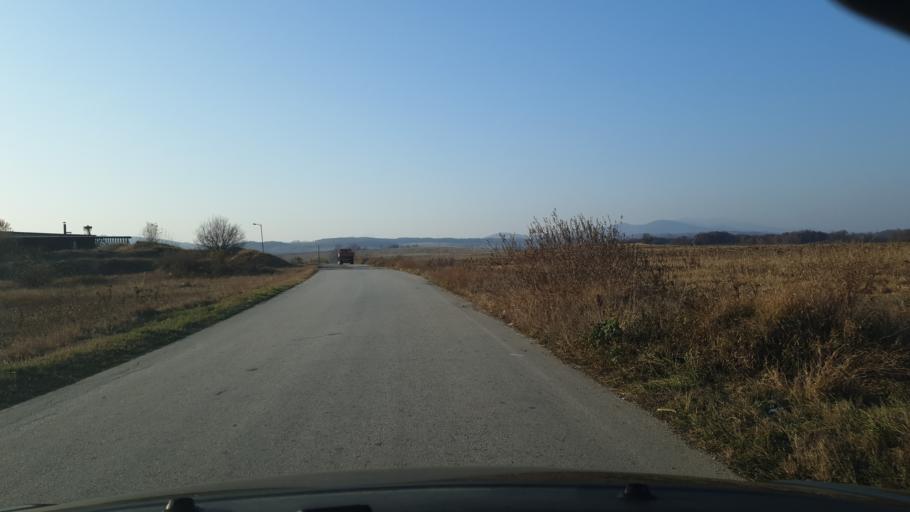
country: RS
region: Central Serbia
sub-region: Zajecarski Okrug
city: Zajecar
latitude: 44.0914
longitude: 22.3407
